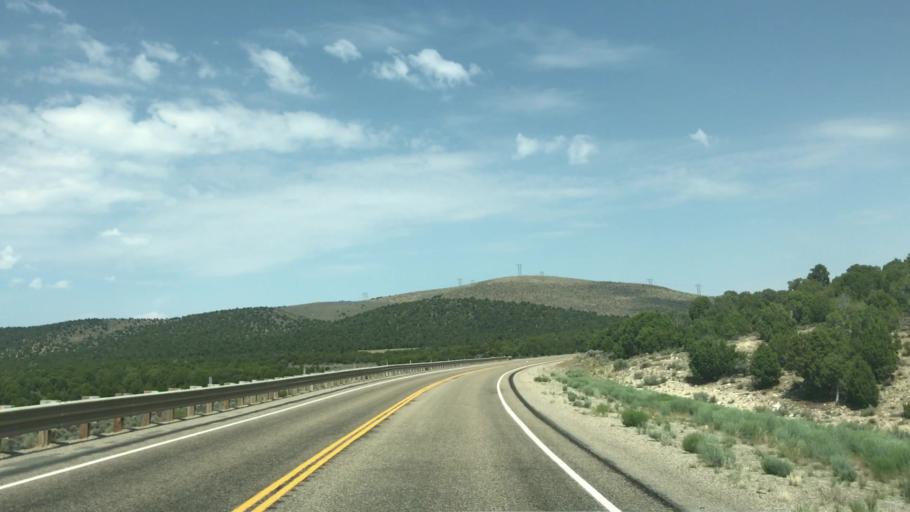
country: US
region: Nevada
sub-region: White Pine County
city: Ely
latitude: 39.3913
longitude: -115.0806
